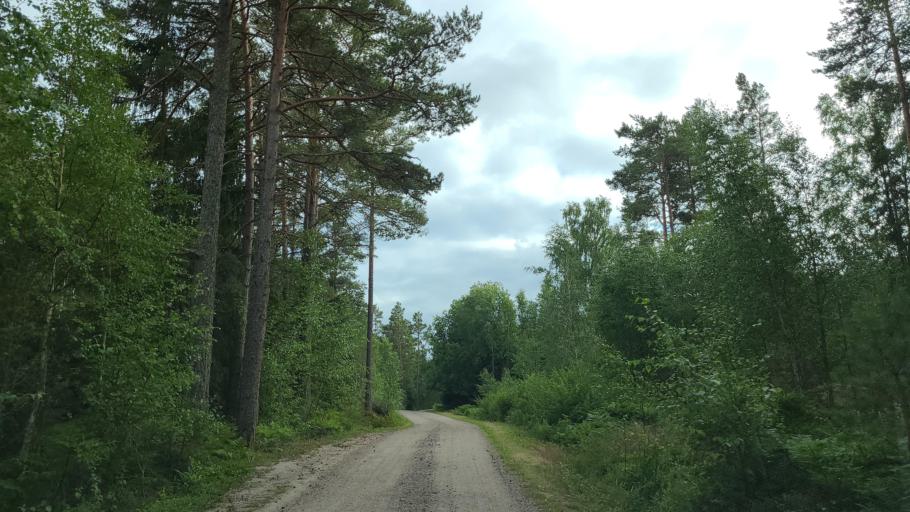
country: FI
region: Varsinais-Suomi
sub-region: Aboland-Turunmaa
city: Nagu
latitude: 60.1353
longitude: 21.8025
